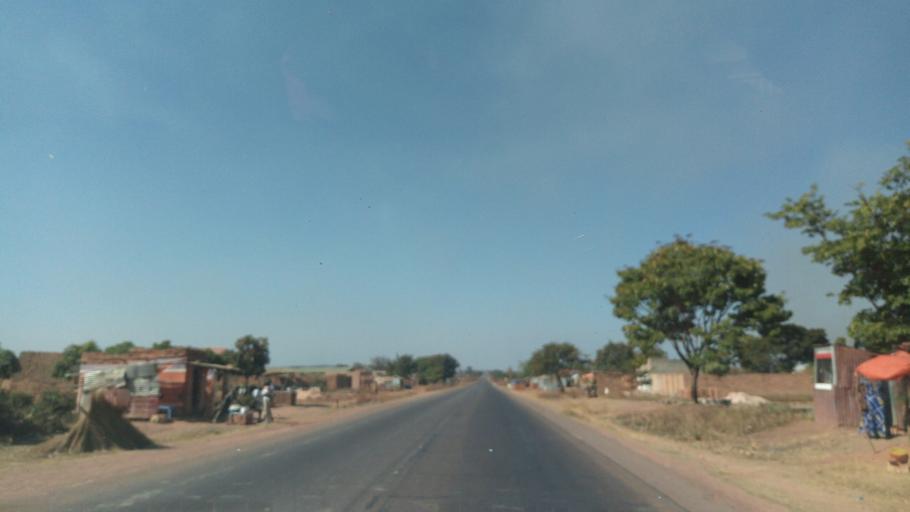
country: CD
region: Katanga
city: Lubumbashi
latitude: -11.5695
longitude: 27.5488
